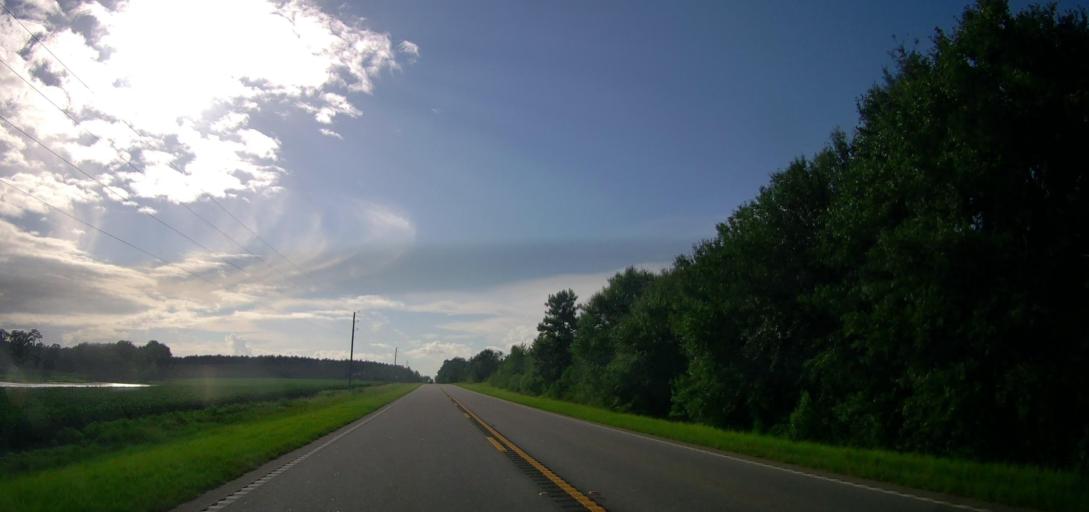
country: US
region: Georgia
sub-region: Coffee County
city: Douglas
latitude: 31.4764
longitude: -82.7847
